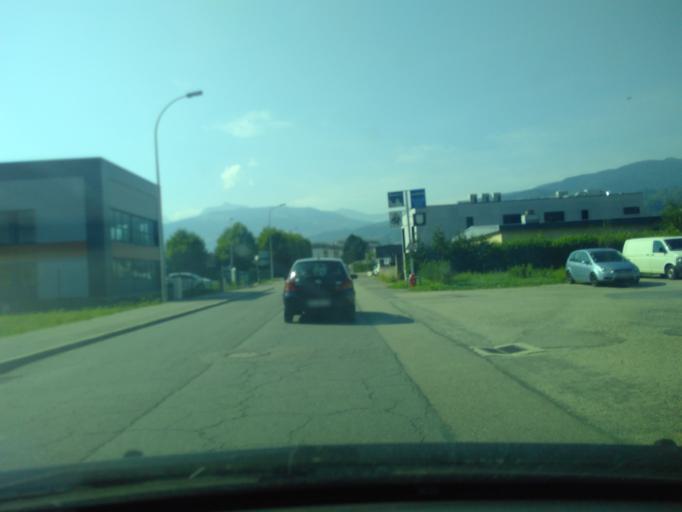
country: FR
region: Rhone-Alpes
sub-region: Departement de la Haute-Savoie
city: Sallanches
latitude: 45.9515
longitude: 6.6317
